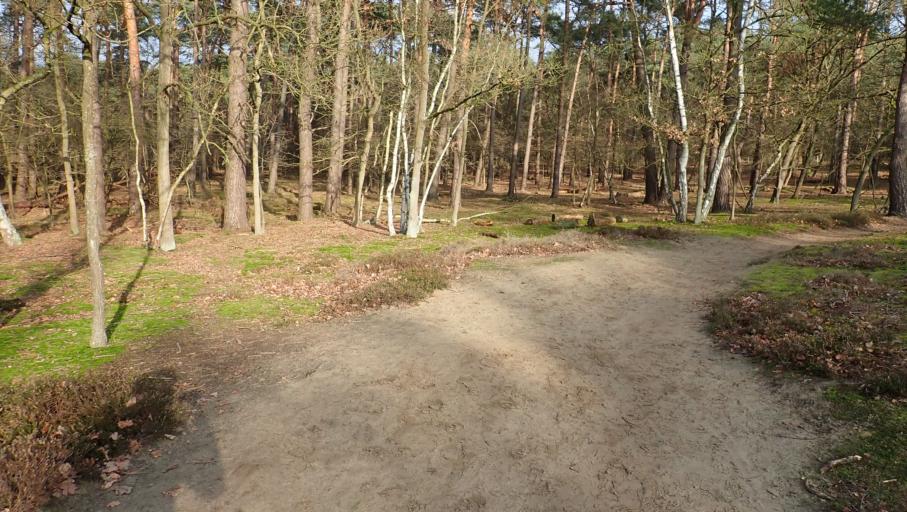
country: BE
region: Flanders
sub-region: Provincie Vlaams-Brabant
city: Tremelo
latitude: 51.0129
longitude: 4.7179
